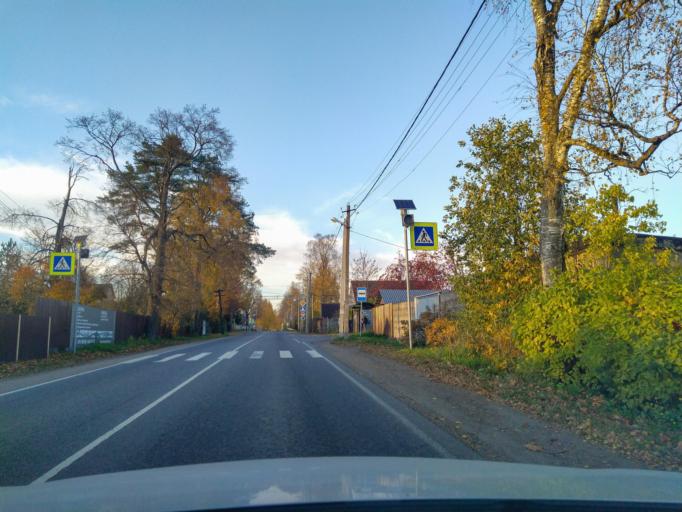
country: RU
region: Leningrad
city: Kobrinskoye
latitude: 59.4267
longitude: 30.1153
